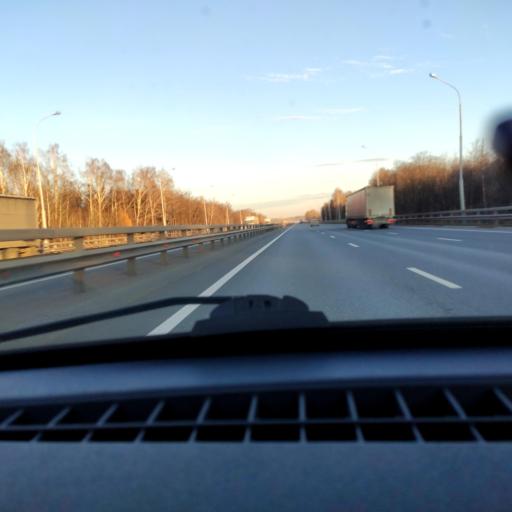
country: RU
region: Bashkortostan
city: Ufa
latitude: 54.6483
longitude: 56.0414
